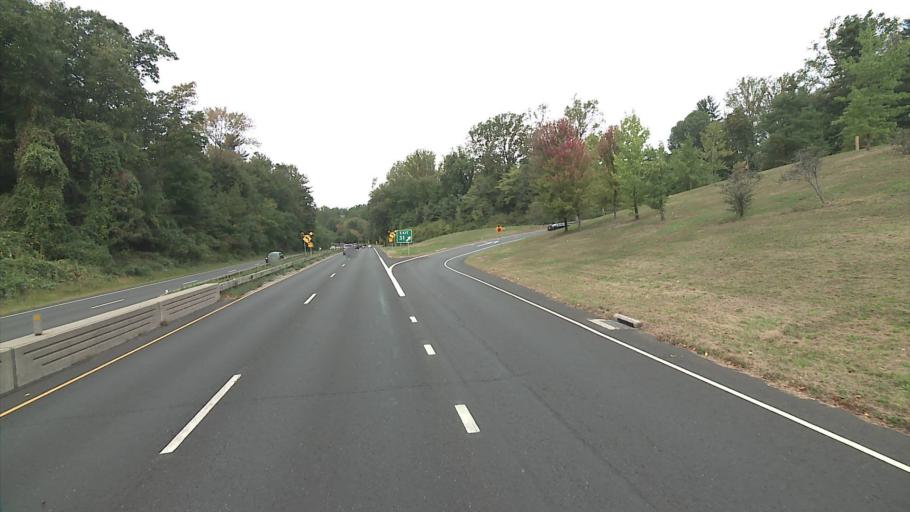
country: US
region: Connecticut
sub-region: Fairfield County
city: Glenville
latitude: 41.0950
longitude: -73.6329
